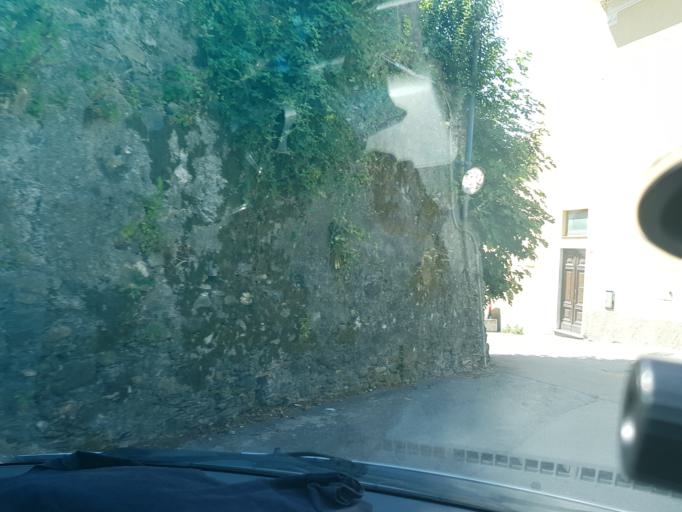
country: IT
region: Liguria
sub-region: Provincia di Genova
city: San Teodoro
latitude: 44.4284
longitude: 8.8399
